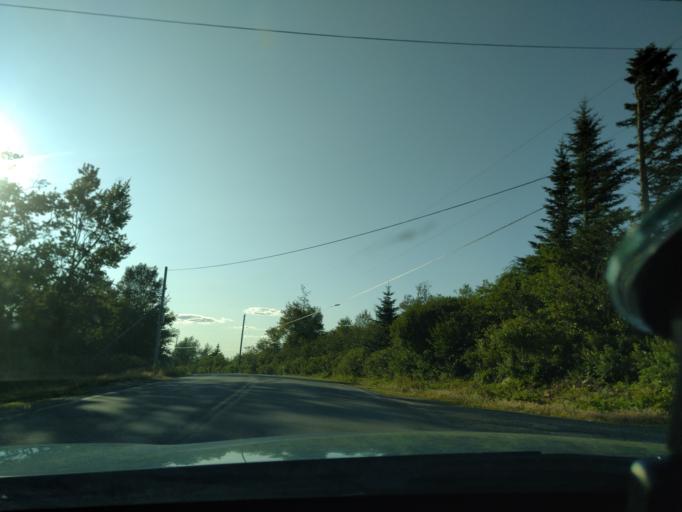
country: US
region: Maine
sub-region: Washington County
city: Machiasport
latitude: 44.6683
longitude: -67.2398
